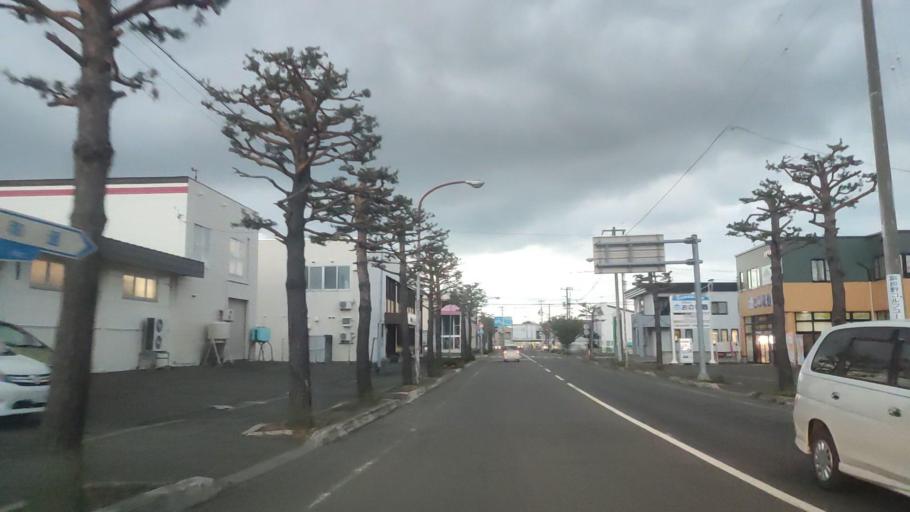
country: JP
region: Hokkaido
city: Shimo-furano
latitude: 43.3399
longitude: 142.3914
